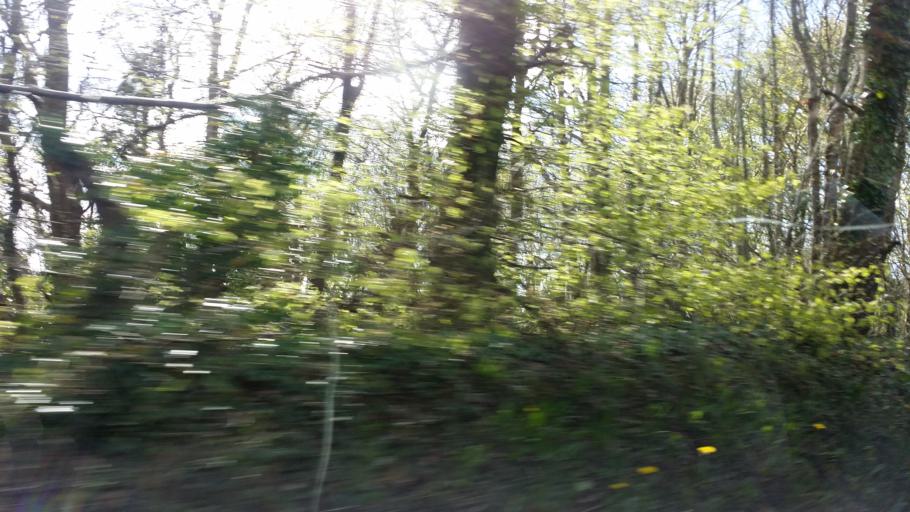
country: IE
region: Ulster
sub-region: County Donegal
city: Ballyshannon
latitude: 54.4892
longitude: -8.1447
